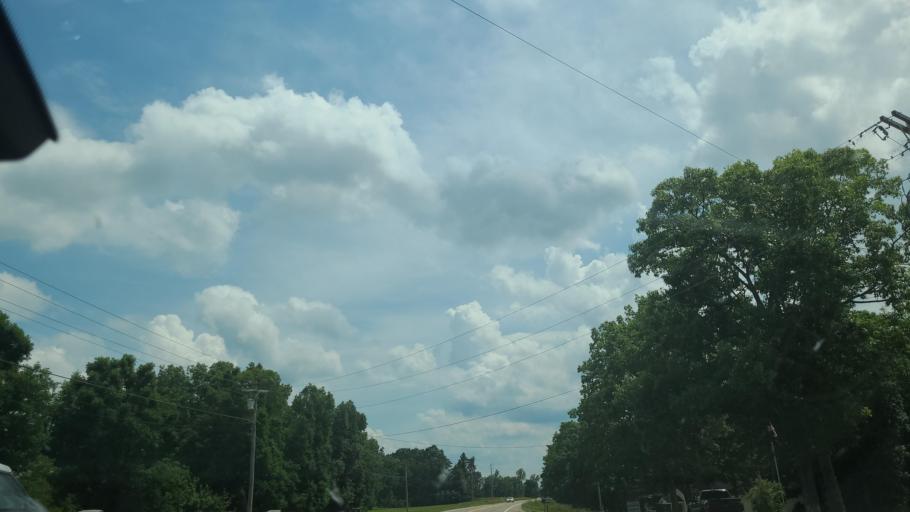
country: US
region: Tennessee
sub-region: Cumberland County
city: Lake Tansi
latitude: 35.8707
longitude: -85.0040
